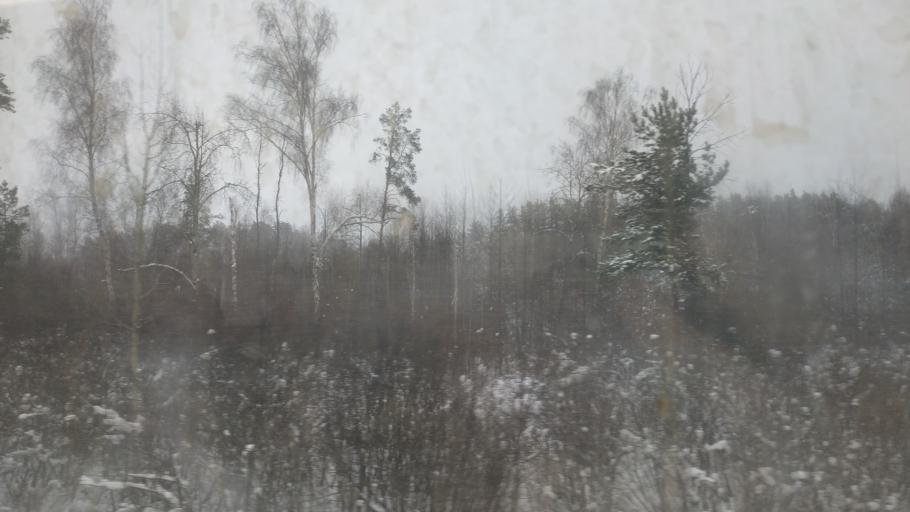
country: RU
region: Moskovskaya
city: Malyshevo
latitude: 55.5188
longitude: 38.3316
